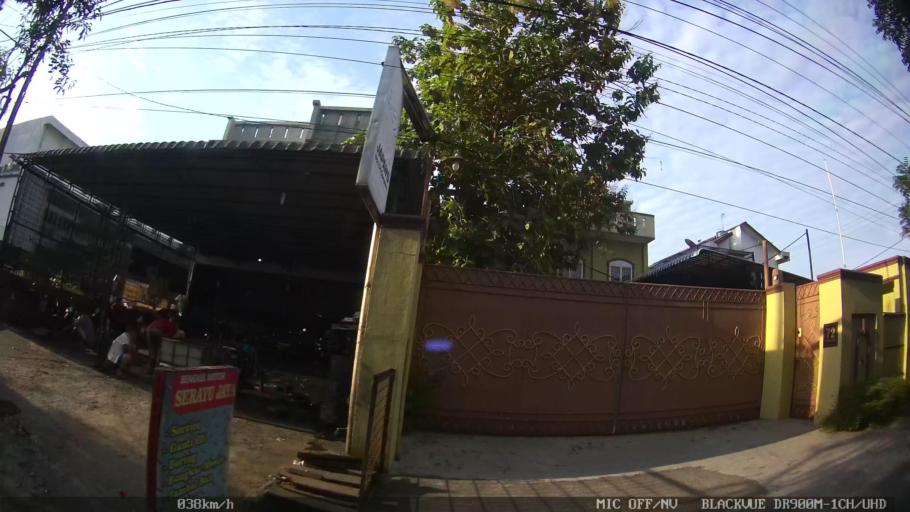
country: ID
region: North Sumatra
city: Medan
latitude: 3.5773
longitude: 98.6469
